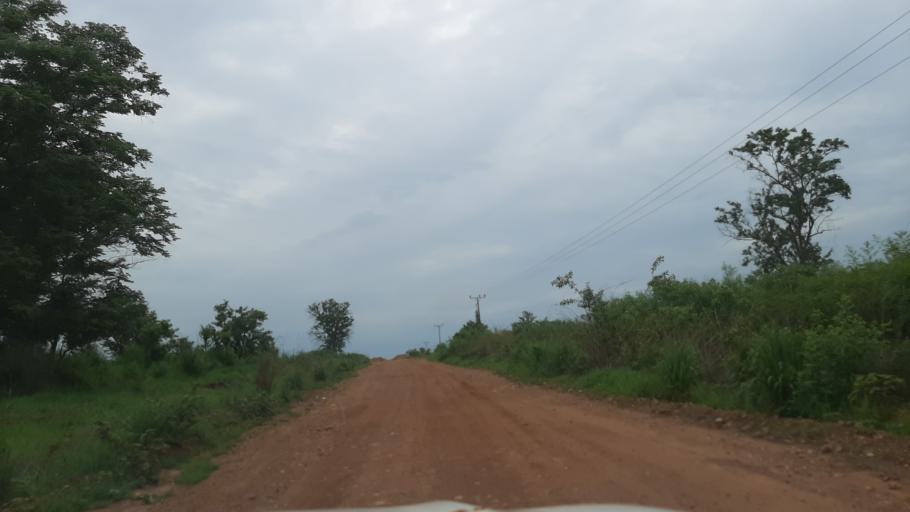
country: ET
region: Gambela
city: Gambela
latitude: 8.2151
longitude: 34.5529
